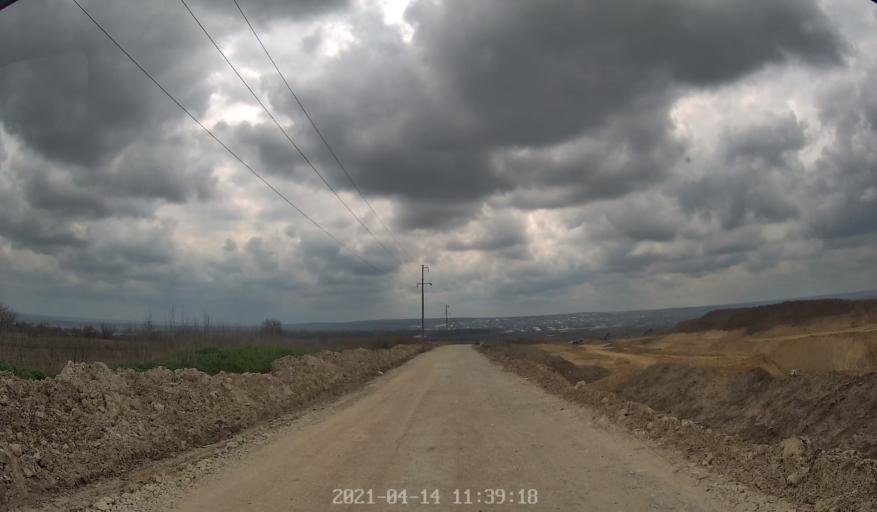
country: MD
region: Criuleni
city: Criuleni
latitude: 47.1681
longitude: 29.1839
